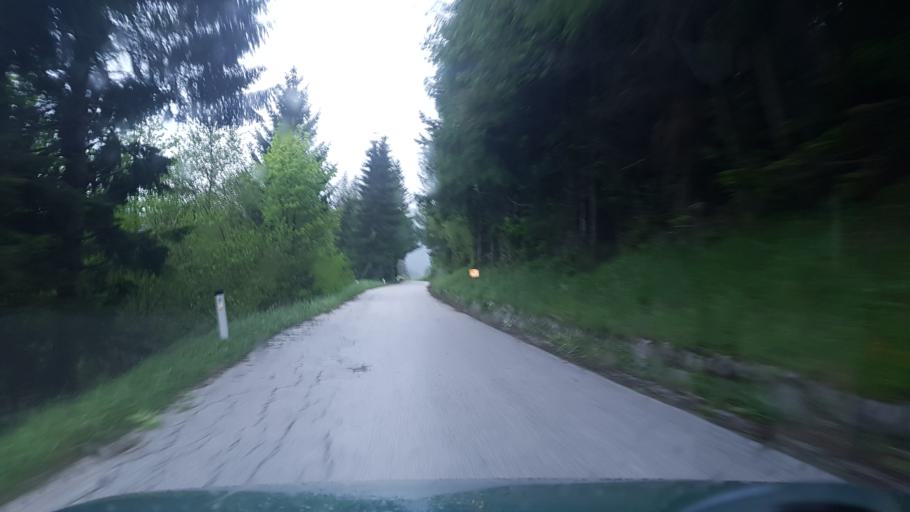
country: SI
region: Bohinj
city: Bohinjska Bistrica
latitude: 46.2246
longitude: 14.0272
